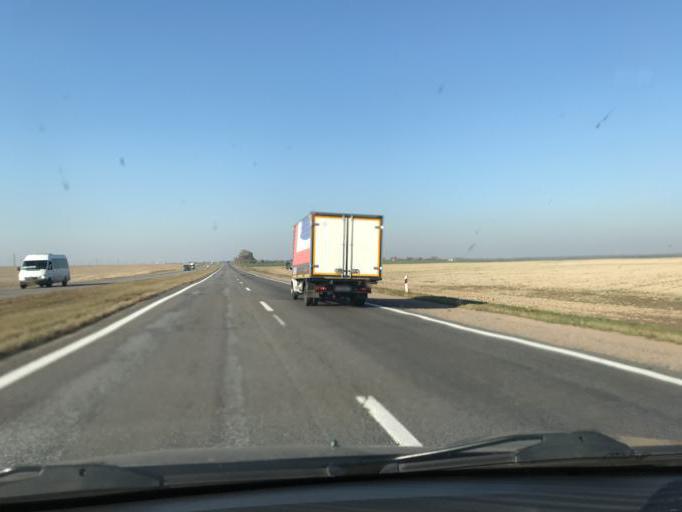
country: BY
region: Minsk
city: Dukora
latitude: 53.6886
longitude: 27.9073
